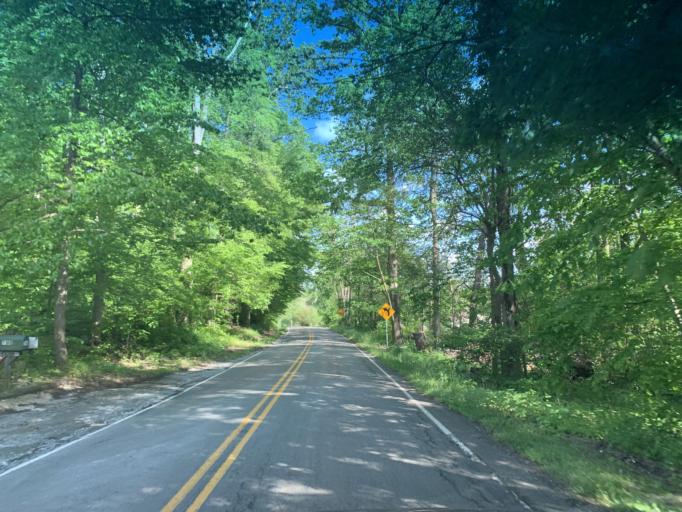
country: US
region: Maryland
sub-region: Cecil County
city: Rising Sun
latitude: 39.6925
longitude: -76.1489
